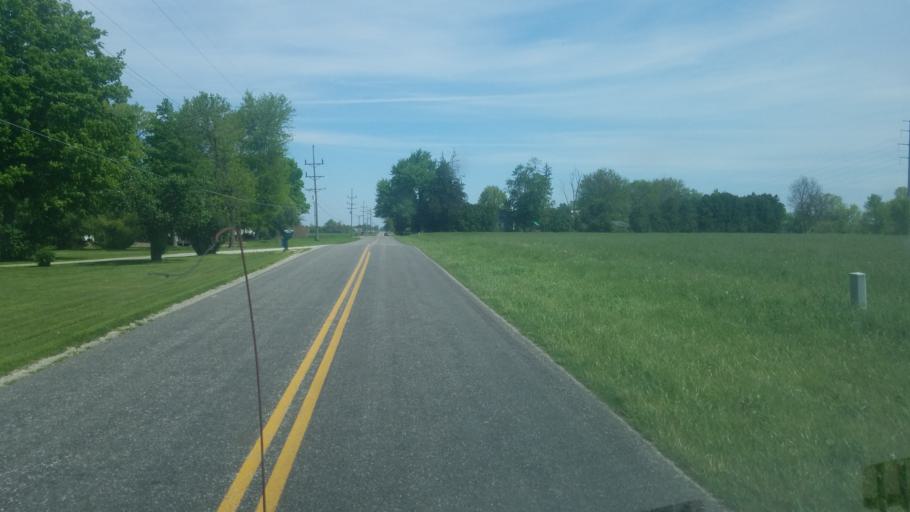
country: US
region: Ohio
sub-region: Seneca County
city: Tiffin
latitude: 41.1011
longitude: -83.1313
